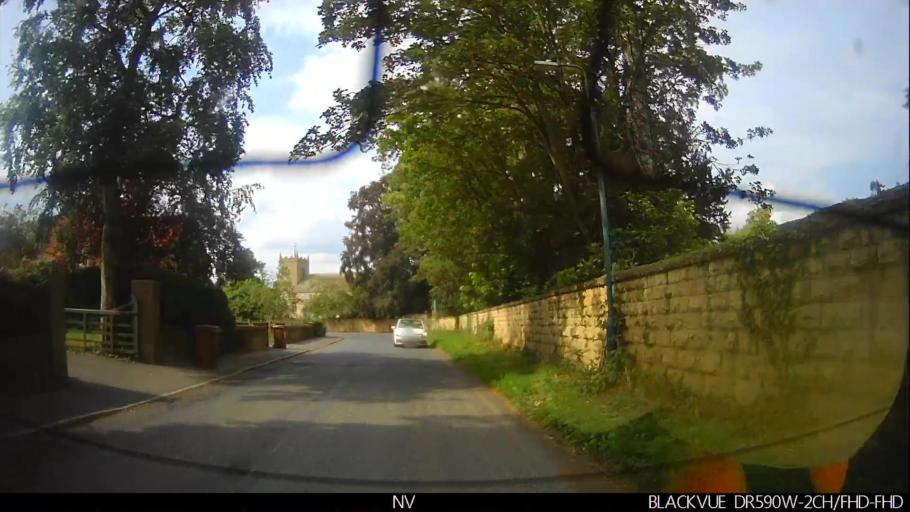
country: GB
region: England
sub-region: North Yorkshire
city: Great Habton
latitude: 54.2052
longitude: -0.8025
